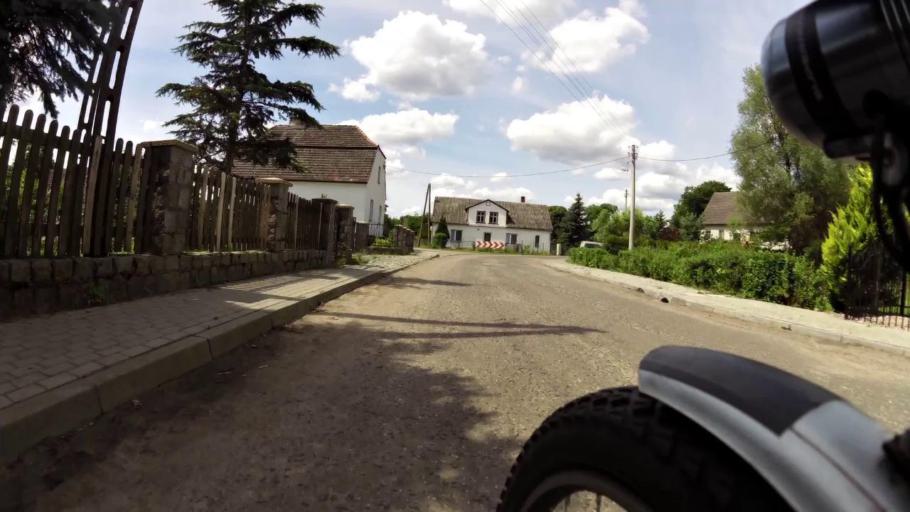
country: PL
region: West Pomeranian Voivodeship
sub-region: Powiat lobeski
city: Wegorzyno
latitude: 53.5211
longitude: 15.4445
